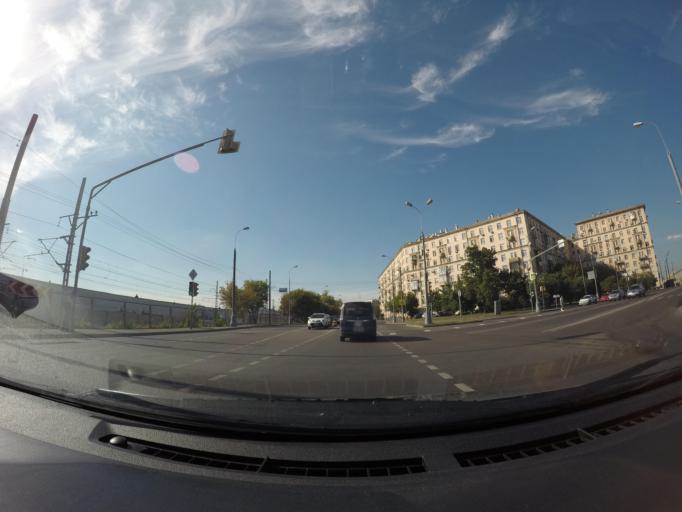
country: RU
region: Moscow
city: Mar'ina Roshcha
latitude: 55.8001
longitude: 37.6344
